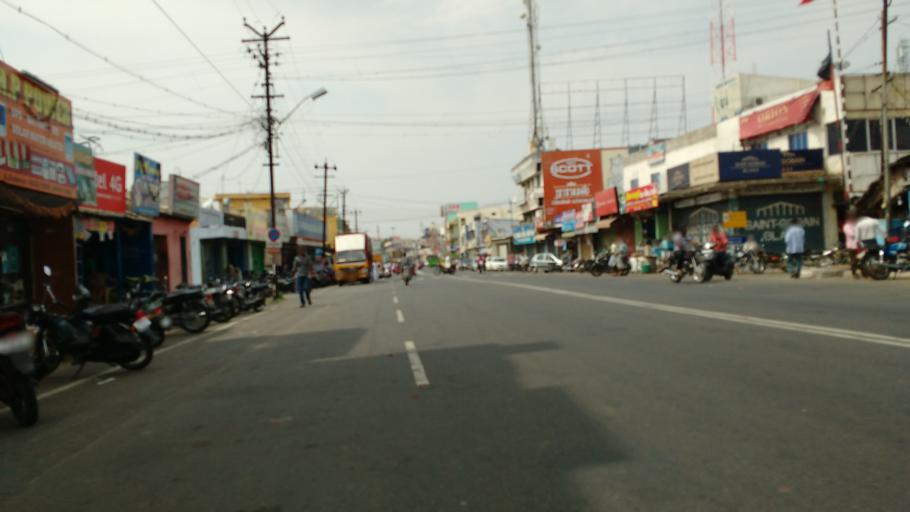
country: IN
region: Tamil Nadu
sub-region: Erode
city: Gobichettipalayam
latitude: 11.4548
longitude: 77.4402
